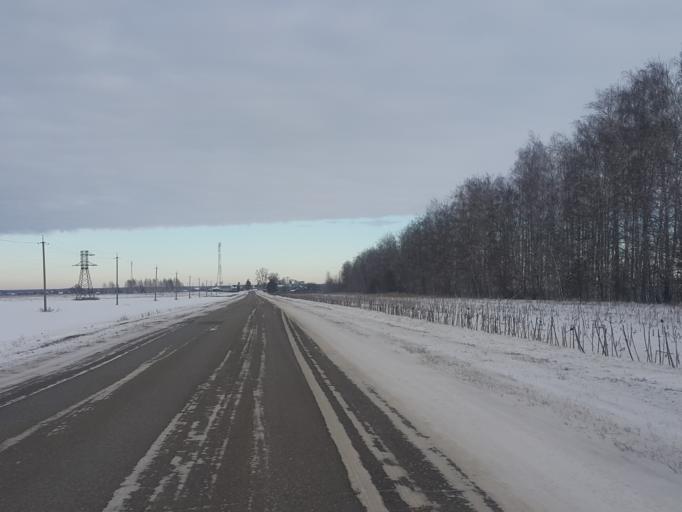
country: RU
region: Tambov
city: Rasskazovo
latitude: 52.8204
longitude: 41.7989
